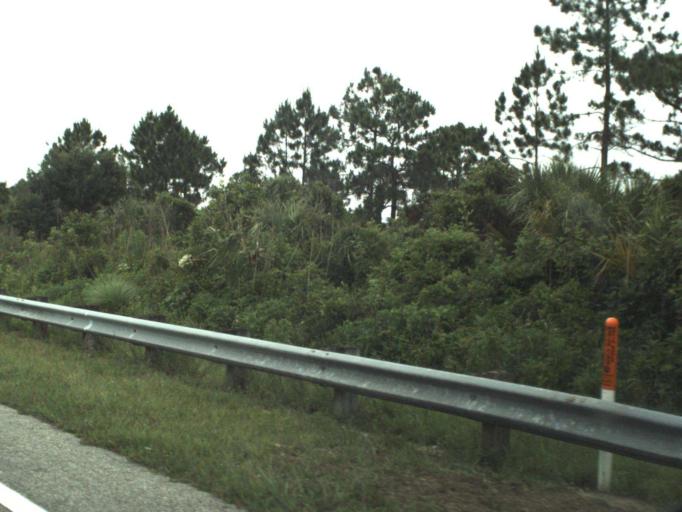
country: US
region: Florida
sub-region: Brevard County
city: Titusville
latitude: 28.5509
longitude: -80.8749
